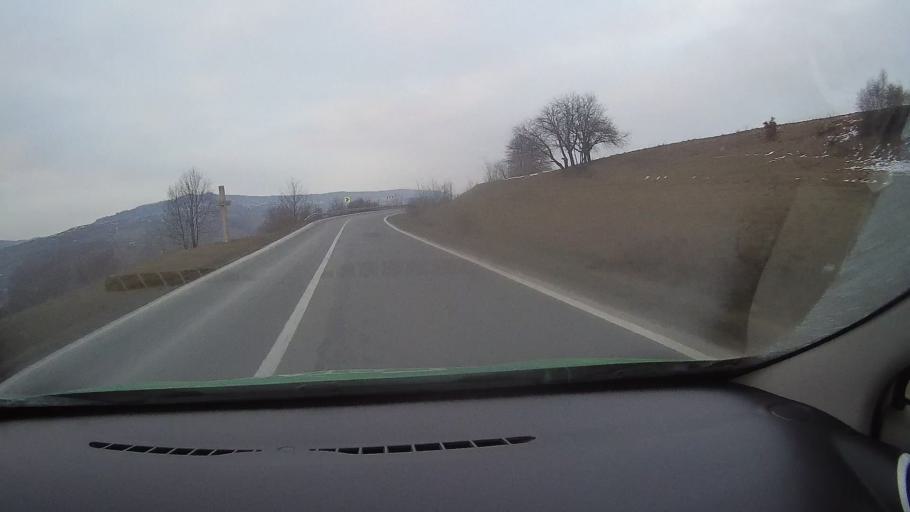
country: RO
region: Harghita
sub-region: Comuna Lupeni
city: Lupeni
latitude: 46.3584
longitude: 25.2474
